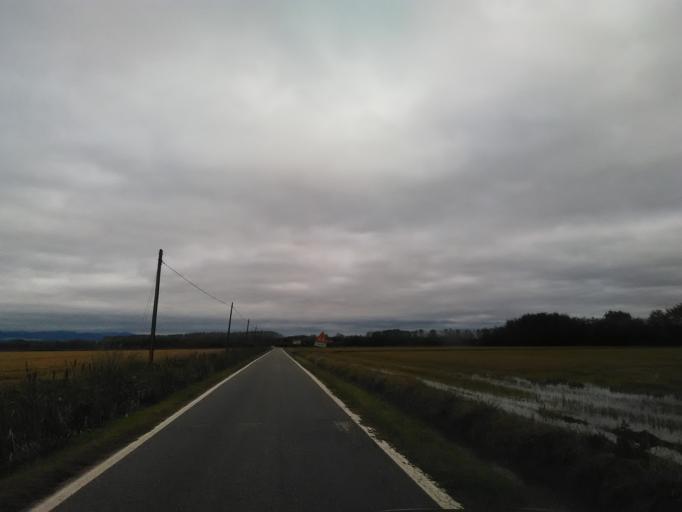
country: IT
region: Piedmont
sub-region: Provincia di Vercelli
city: San Germano Vercellese
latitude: 45.3944
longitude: 8.2424
